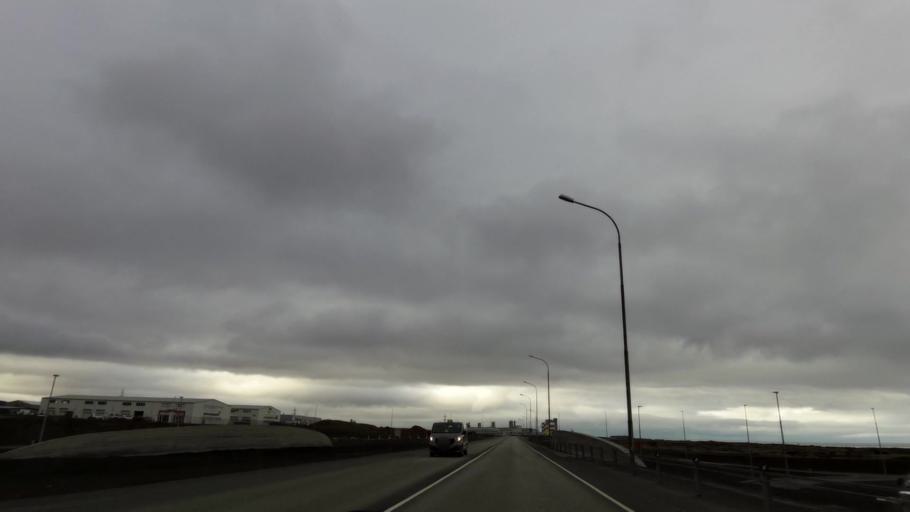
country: IS
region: Capital Region
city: Alftanes
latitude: 64.0513
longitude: -21.9942
